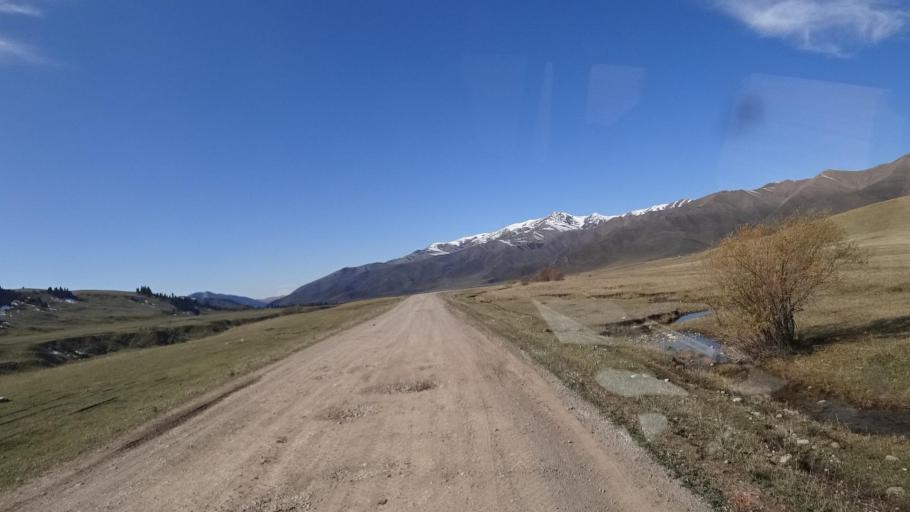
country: KZ
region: Almaty Oblysy
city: Kegen
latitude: 42.7350
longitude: 79.0197
